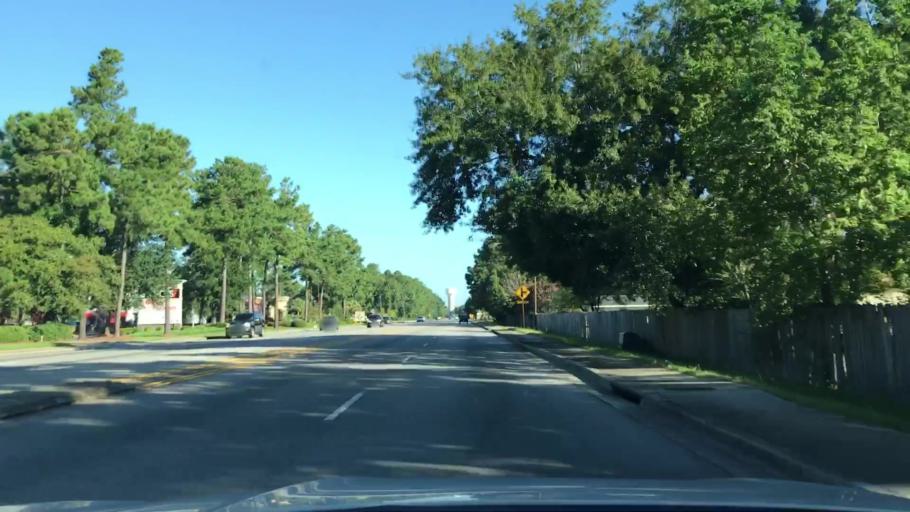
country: US
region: South Carolina
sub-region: Berkeley County
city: Goose Creek
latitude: 33.0236
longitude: -80.0546
